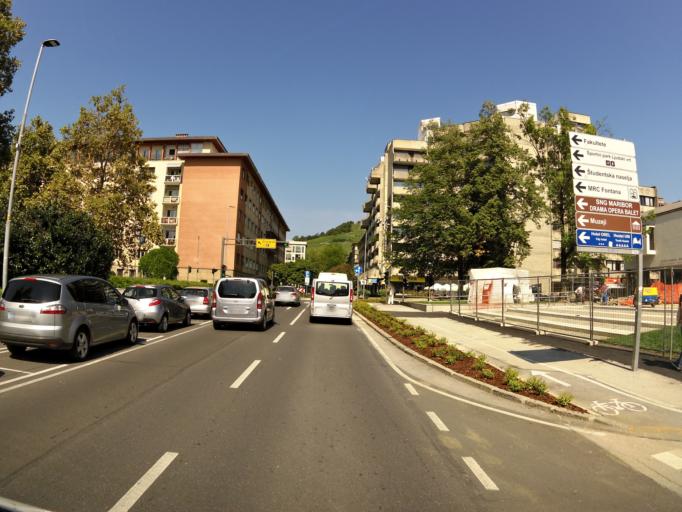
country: SI
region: Maribor
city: Maribor
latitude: 46.5615
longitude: 15.6517
